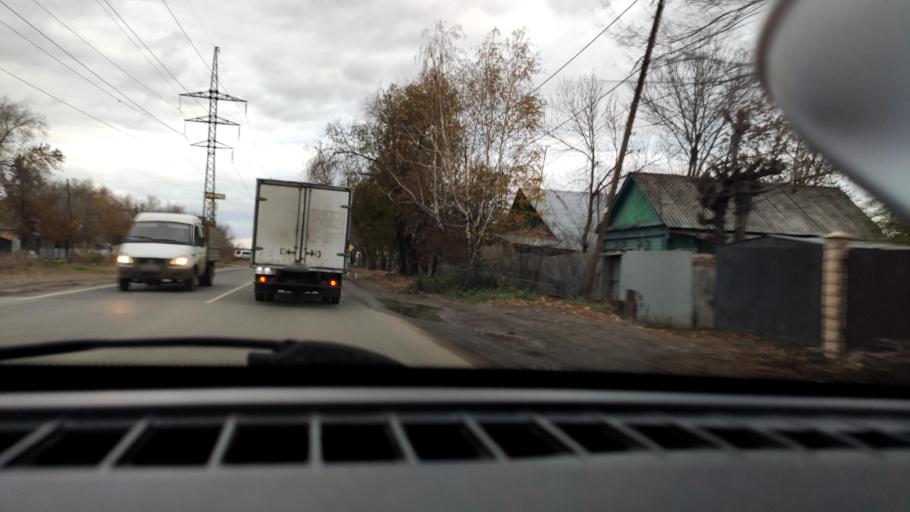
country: RU
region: Samara
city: Samara
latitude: 53.1326
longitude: 50.1333
